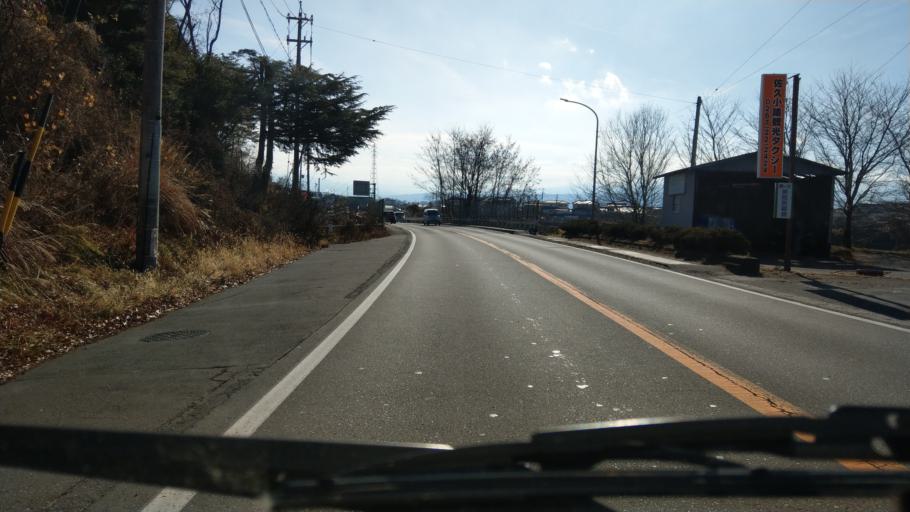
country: JP
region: Nagano
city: Komoro
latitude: 36.3114
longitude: 138.4427
